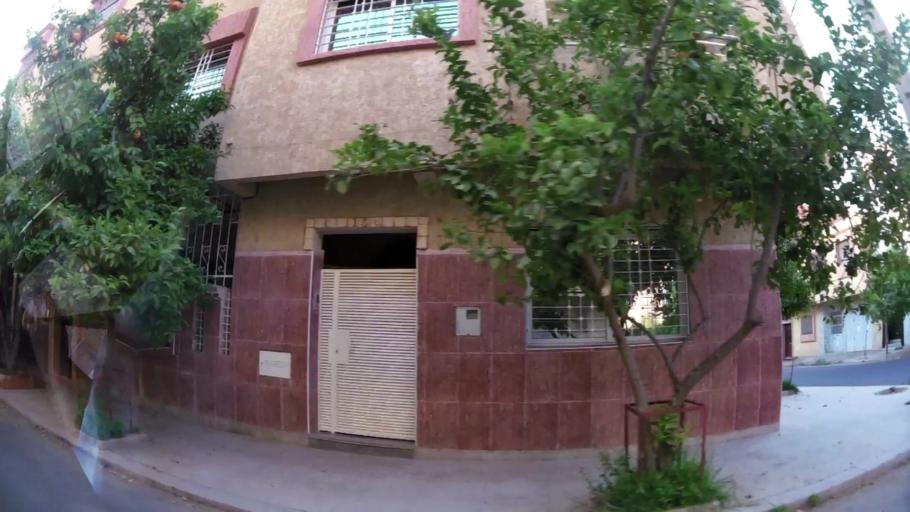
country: MA
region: Oriental
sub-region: Oujda-Angad
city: Oujda
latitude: 34.7107
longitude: -1.9226
